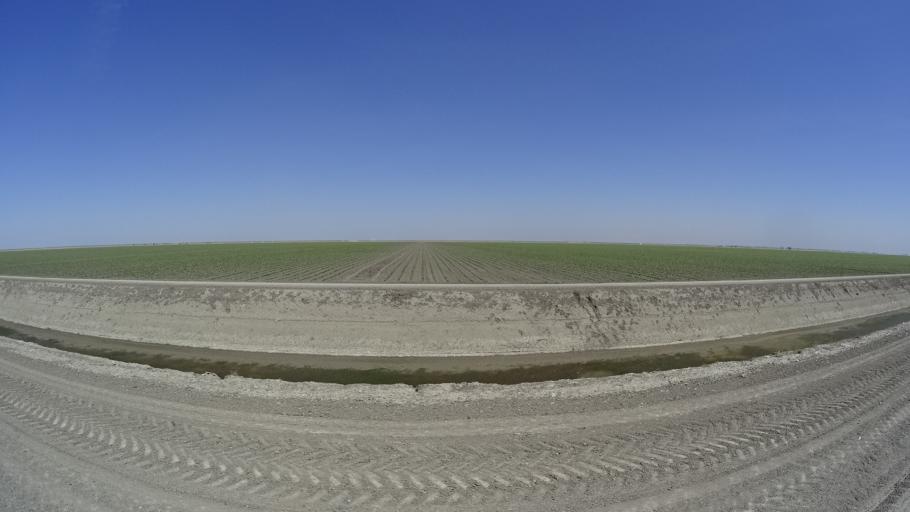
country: US
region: California
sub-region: Kings County
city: Corcoran
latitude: 36.0214
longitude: -119.6732
